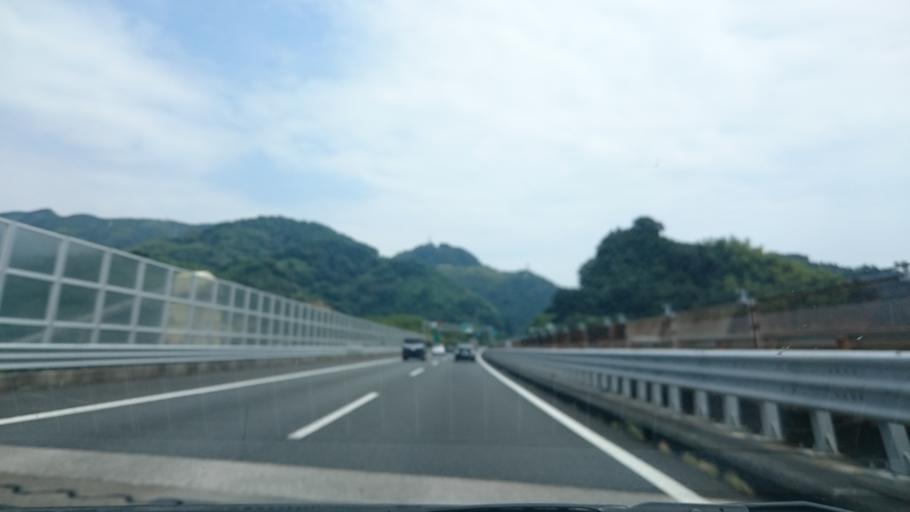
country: JP
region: Shizuoka
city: Shizuoka-shi
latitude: 35.0651
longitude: 138.5264
